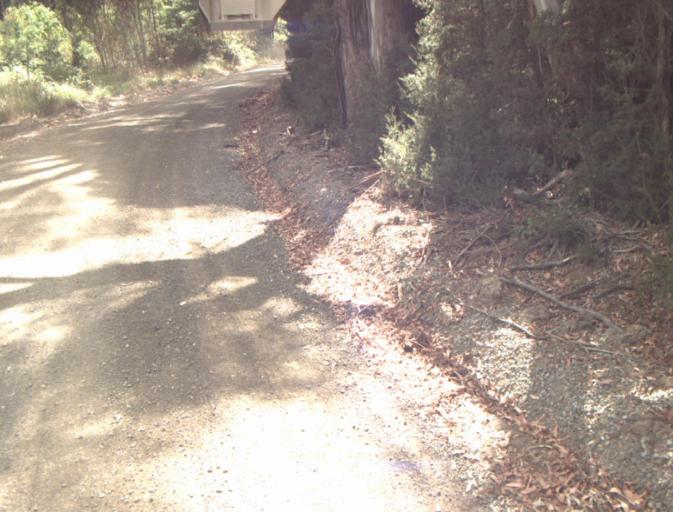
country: AU
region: Tasmania
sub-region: Launceston
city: Mayfield
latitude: -41.2740
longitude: 147.2221
